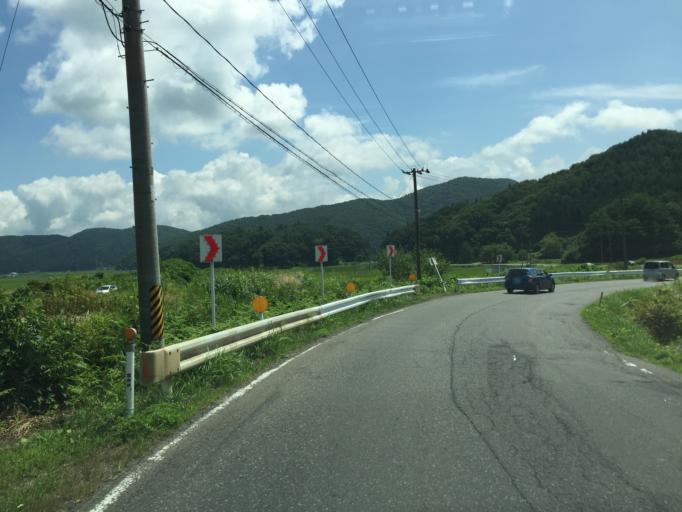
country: JP
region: Fukushima
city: Inawashiro
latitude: 37.4089
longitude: 140.0612
